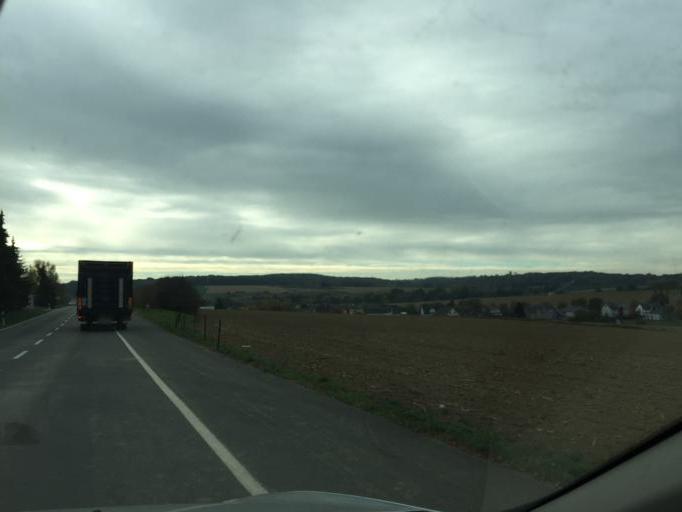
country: LU
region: Luxembourg
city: Capellen
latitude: 49.6203
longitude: 5.9828
